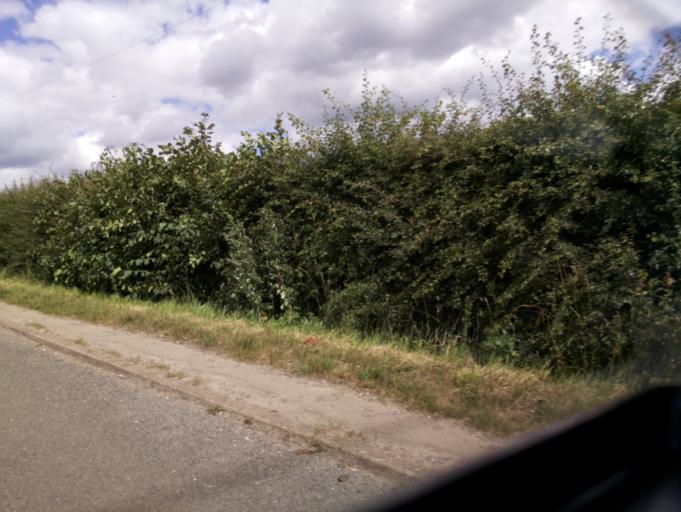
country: GB
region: England
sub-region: Nottinghamshire
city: East Leake
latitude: 52.8377
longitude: -1.1434
